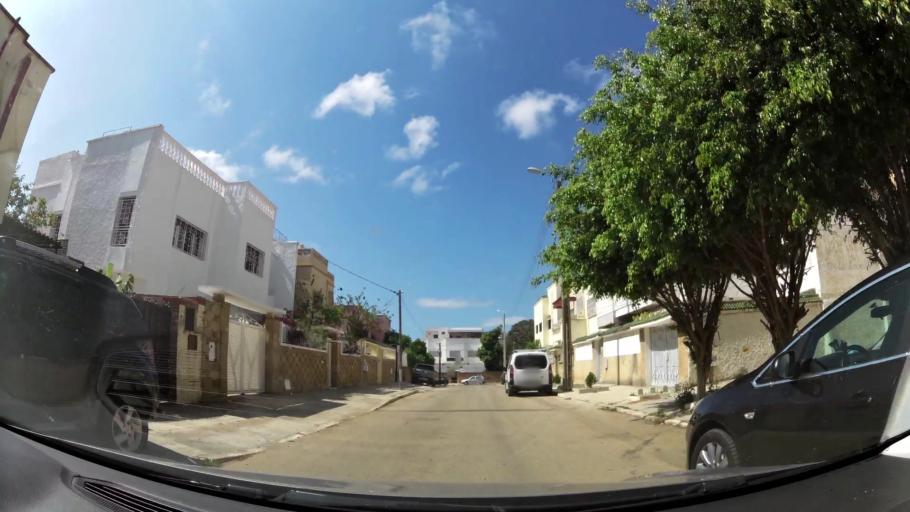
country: MA
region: Rabat-Sale-Zemmour-Zaer
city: Sale
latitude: 34.0366
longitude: -6.7931
